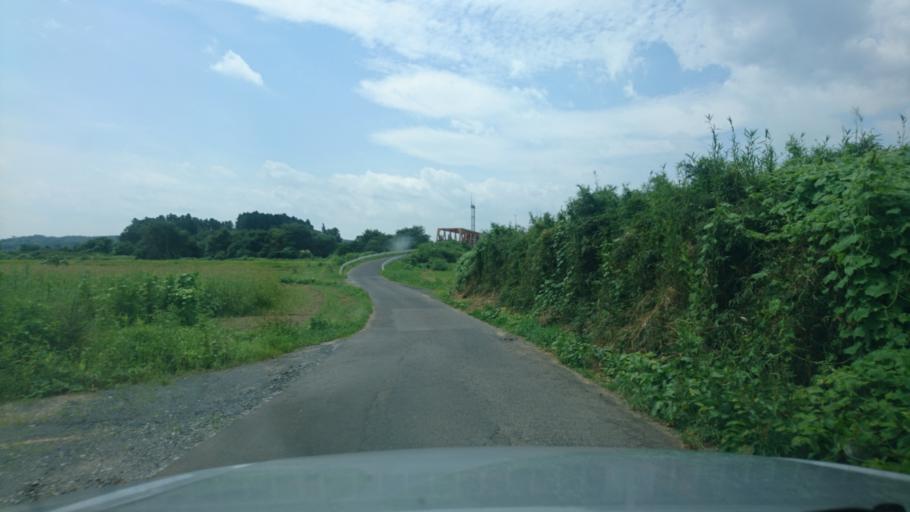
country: JP
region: Iwate
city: Ichinoseki
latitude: 38.7869
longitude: 141.0138
